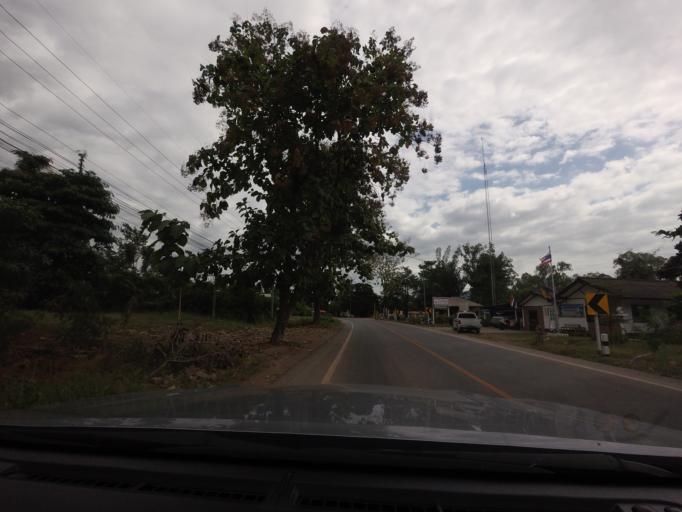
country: TH
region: Phitsanulok
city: Noen Maprang
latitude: 16.6891
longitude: 100.5310
